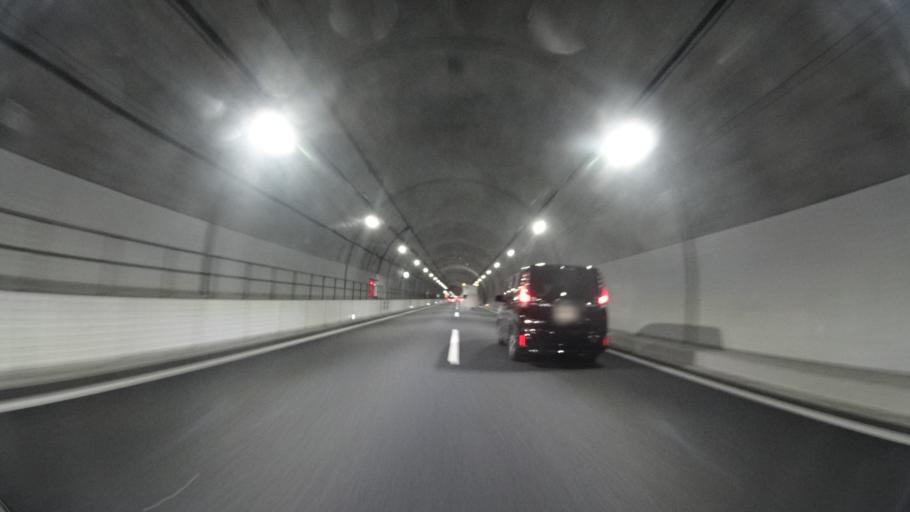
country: JP
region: Mie
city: Kameyama
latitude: 34.9404
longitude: 136.4414
